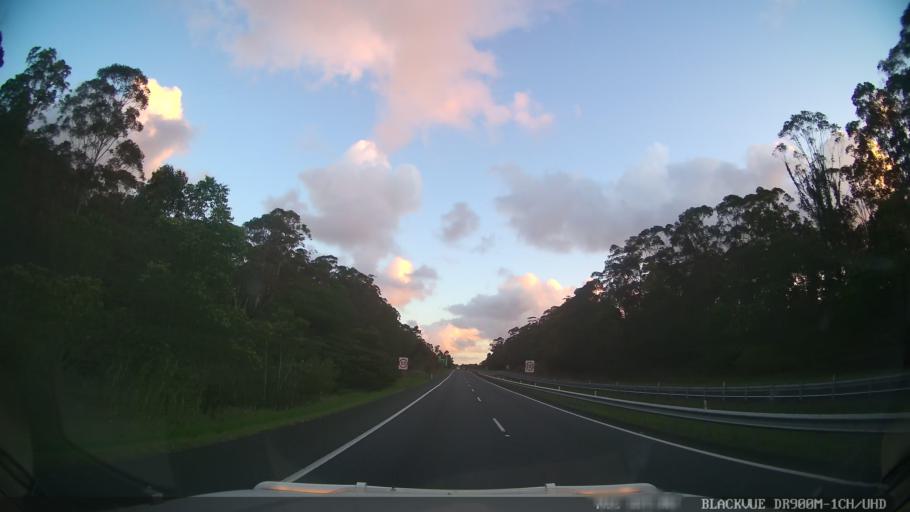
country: AU
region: Queensland
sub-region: Sunshine Coast
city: Twin Waters
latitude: -26.5962
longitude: 152.9716
